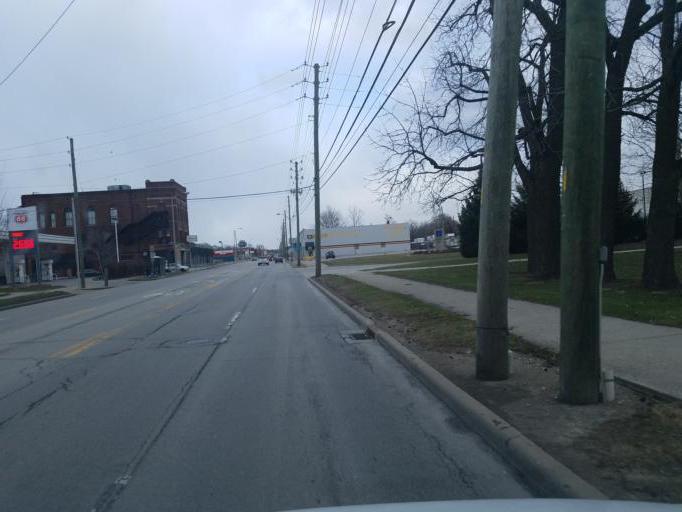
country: US
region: Indiana
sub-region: Marion County
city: Indianapolis
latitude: 39.7676
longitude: -86.1265
